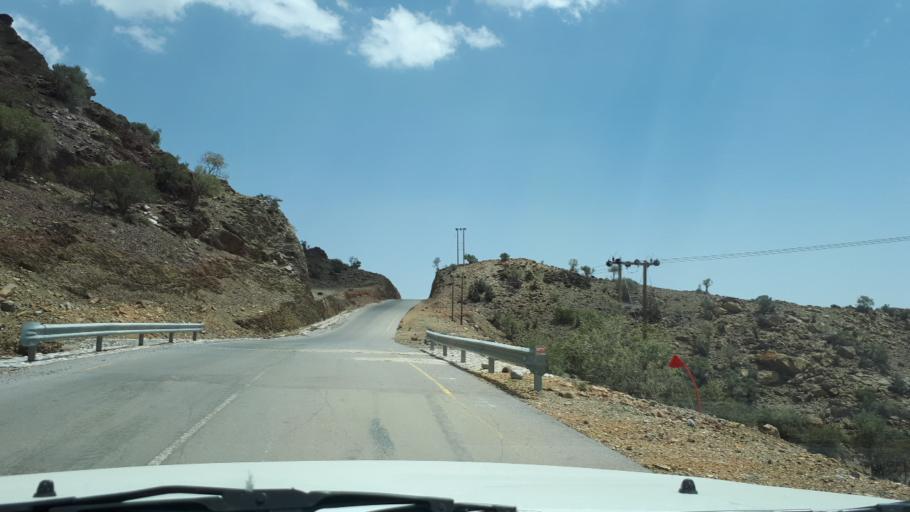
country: OM
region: Al Batinah
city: Rustaq
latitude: 23.2359
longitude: 57.1976
